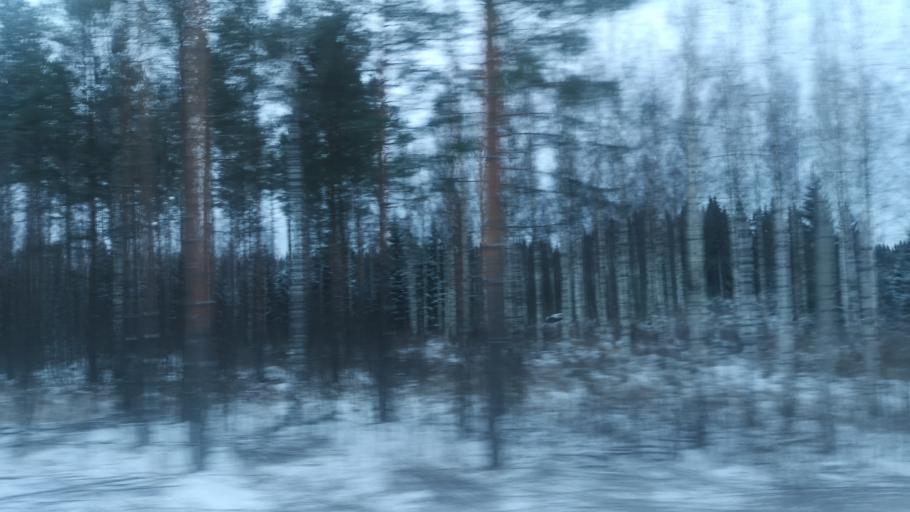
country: FI
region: Southern Savonia
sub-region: Savonlinna
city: Enonkoski
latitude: 62.1047
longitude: 28.6407
